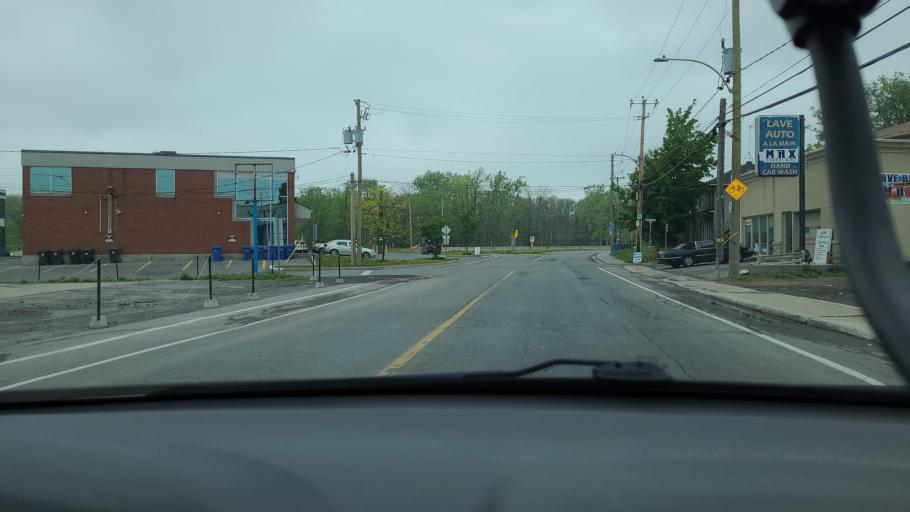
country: CA
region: Quebec
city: Sainte-Anne-de-Bellevue
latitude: 45.3975
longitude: -73.9589
